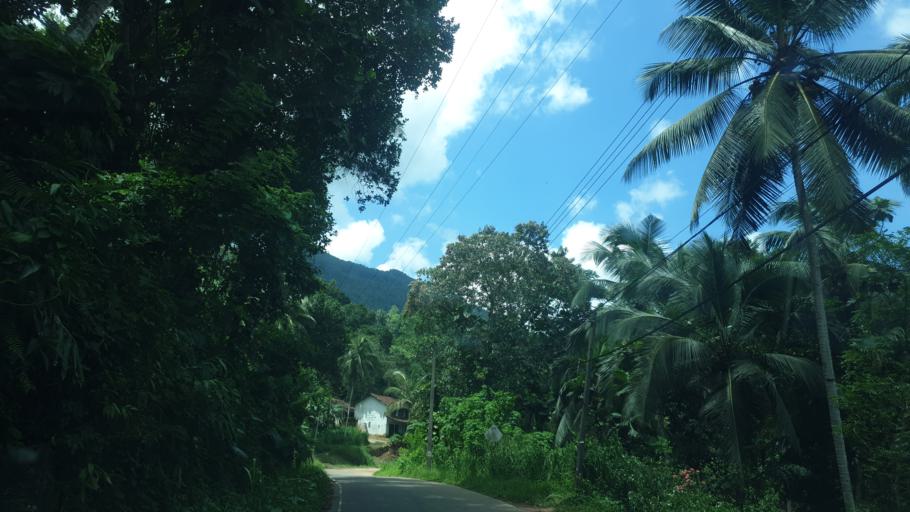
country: LK
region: Sabaragamuwa
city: Ratnapura
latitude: 6.4664
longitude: 80.4280
